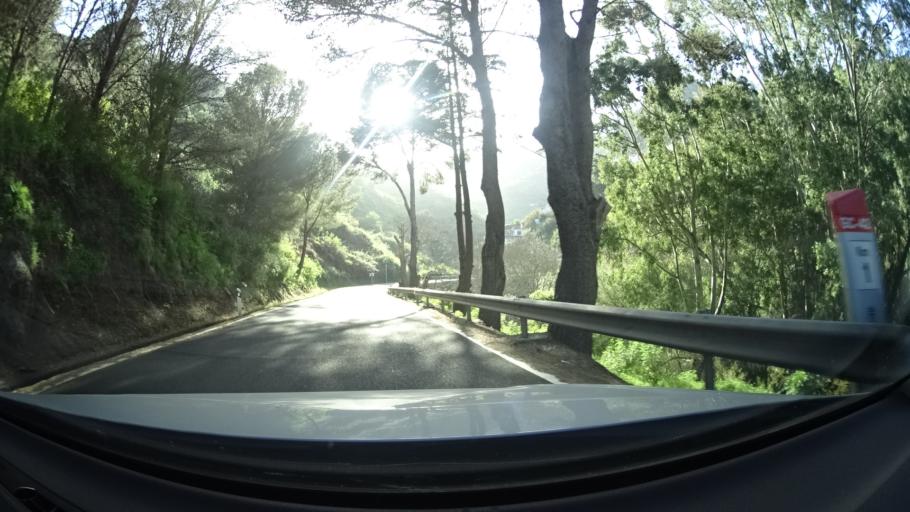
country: ES
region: Canary Islands
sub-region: Provincia de Las Palmas
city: Teror
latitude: 28.0576
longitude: -15.5584
